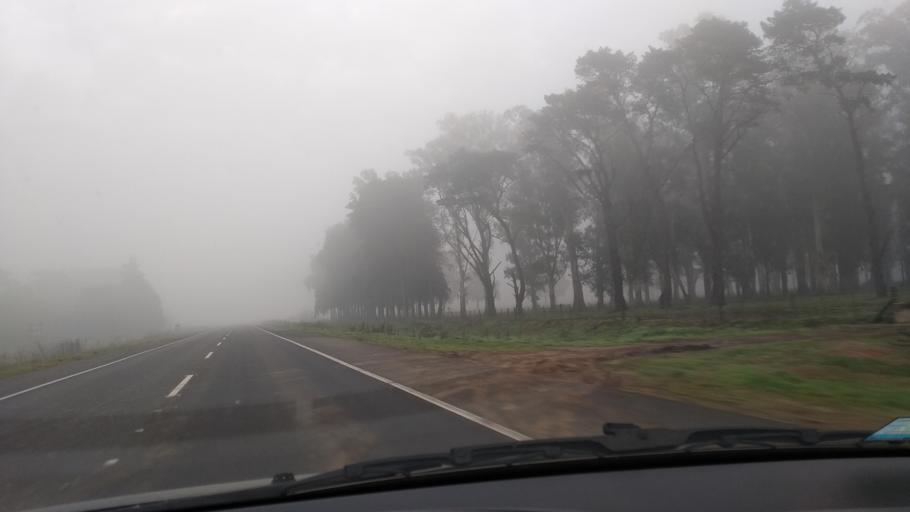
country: AR
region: Buenos Aires
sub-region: Partido de San Vicente
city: San Vicente
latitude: -35.2160
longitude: -58.4260
